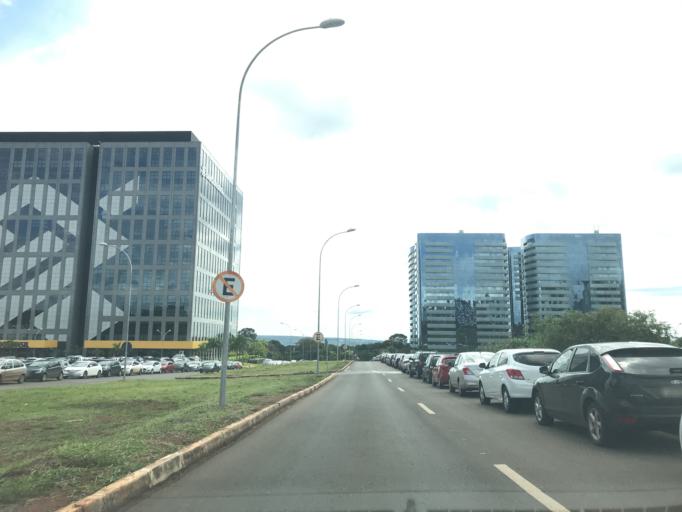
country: BR
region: Federal District
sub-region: Brasilia
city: Brasilia
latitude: -15.7854
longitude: -47.8783
